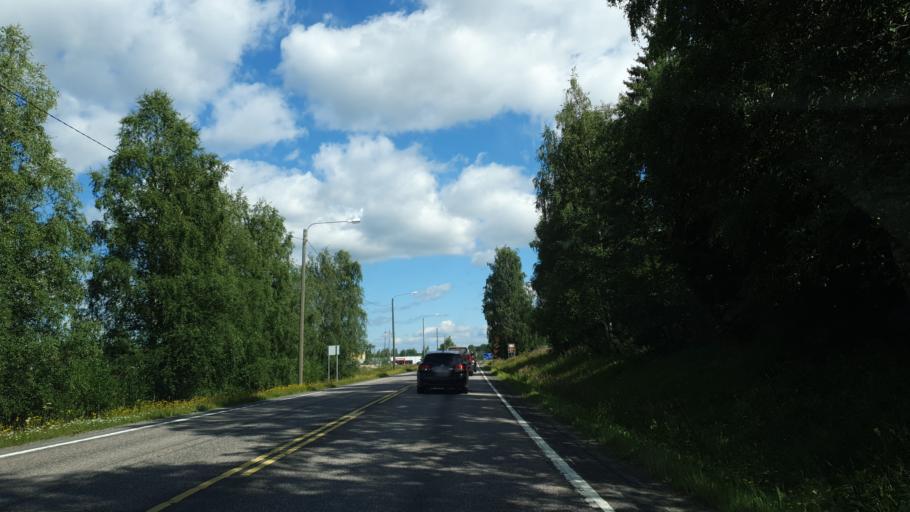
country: FI
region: Central Finland
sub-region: Jaemsae
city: Jaemsae
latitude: 61.8502
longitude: 25.1655
